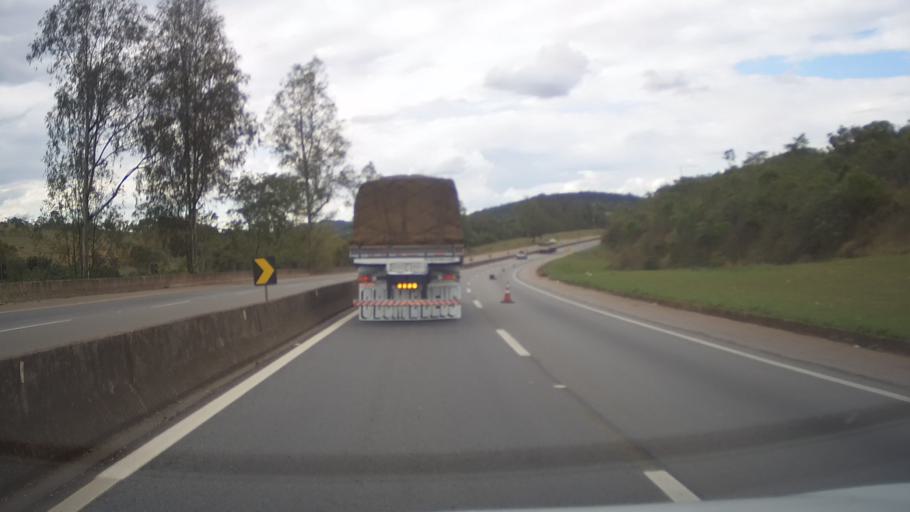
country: BR
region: Minas Gerais
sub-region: Itauna
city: Itauna
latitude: -20.3252
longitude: -44.4566
